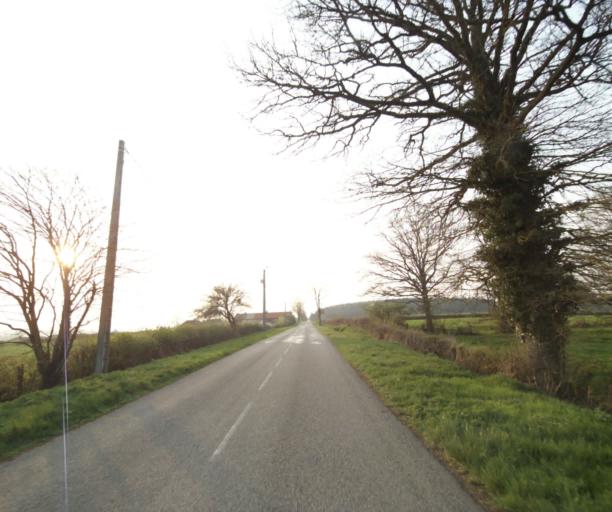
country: FR
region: Bourgogne
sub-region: Departement de Saone-et-Loire
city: Charolles
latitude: 46.4379
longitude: 4.4075
